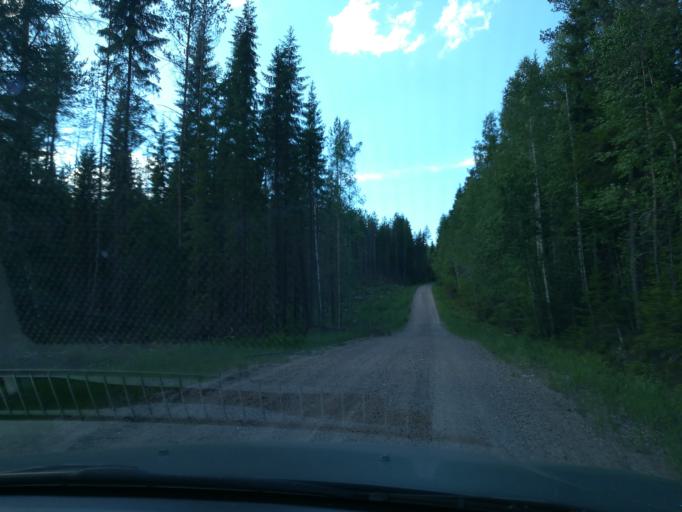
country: FI
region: South Karelia
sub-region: Imatra
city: Ruokolahti
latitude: 61.5404
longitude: 28.8138
